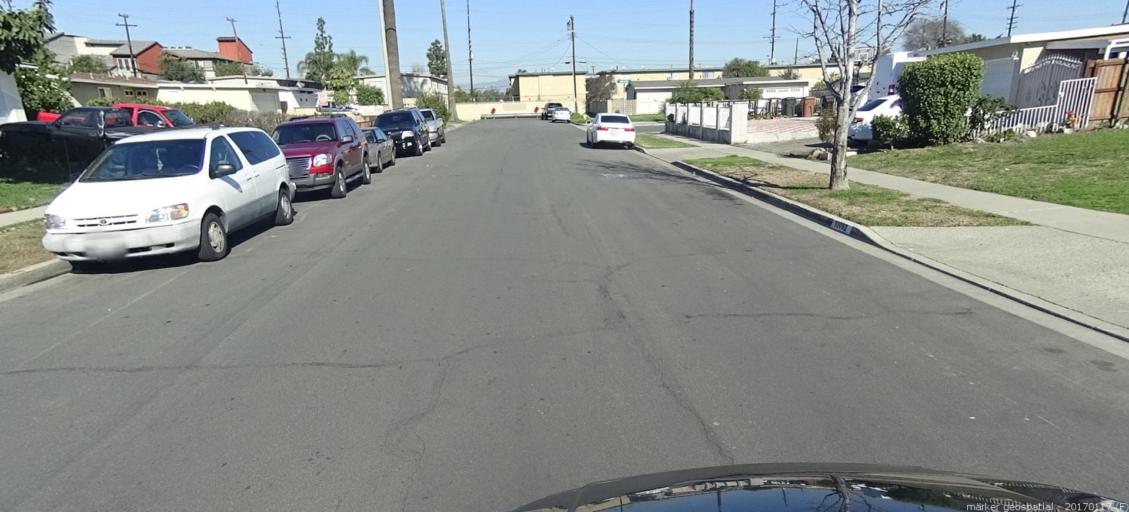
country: US
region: California
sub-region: Orange County
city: Stanton
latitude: 33.8163
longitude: -117.9650
